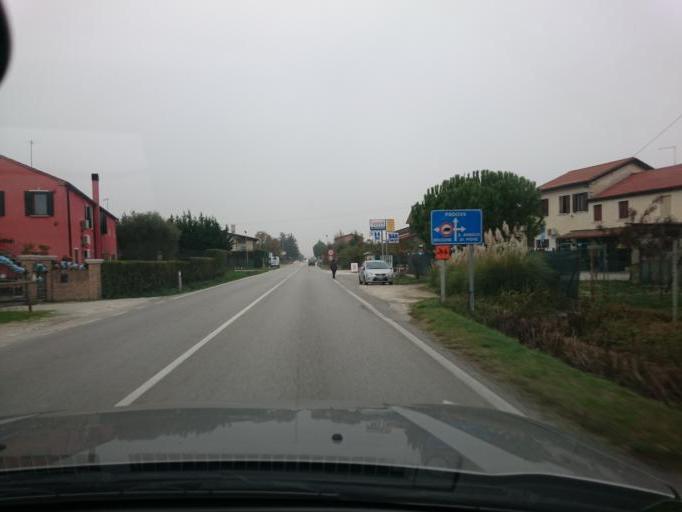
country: IT
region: Veneto
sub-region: Provincia di Padova
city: Sant'Angelo di Piove di Sacco
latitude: 45.3283
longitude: 11.9893
